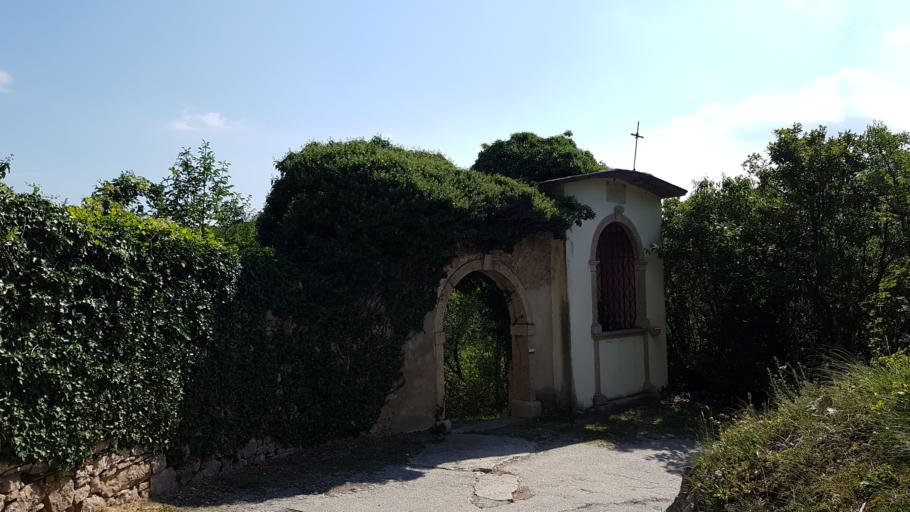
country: IT
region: Trentino-Alto Adige
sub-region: Provincia di Trento
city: Vezzano
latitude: 46.0819
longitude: 10.9912
